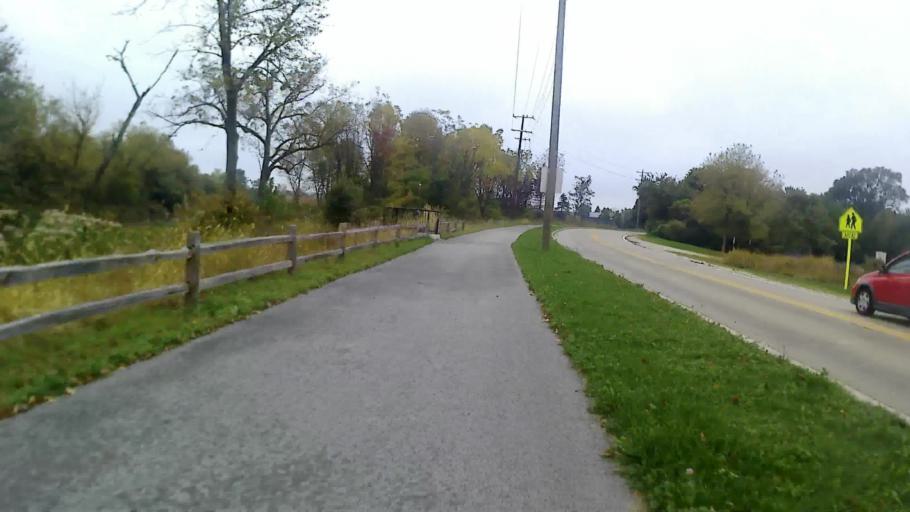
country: US
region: Illinois
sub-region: DuPage County
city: Warrenville
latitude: 41.8112
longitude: -88.1752
